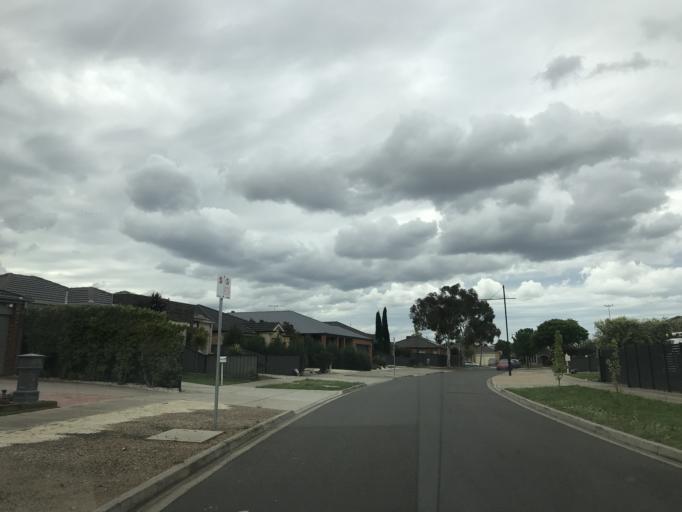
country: AU
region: Victoria
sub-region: Brimbank
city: Derrimut
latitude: -37.7938
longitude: 144.7616
